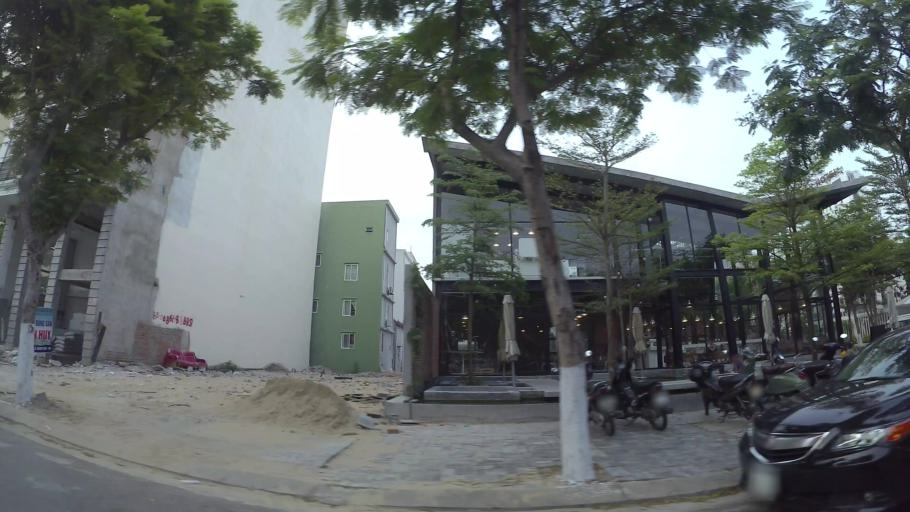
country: VN
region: Da Nang
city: Son Tra
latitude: 16.0479
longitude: 108.2461
